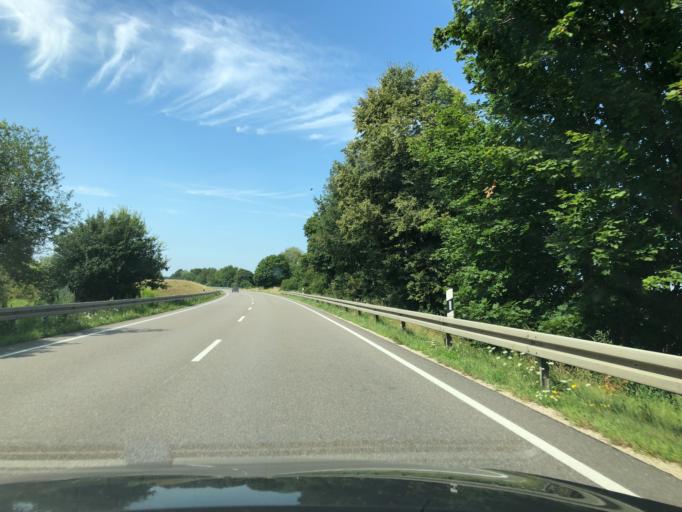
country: DE
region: Bavaria
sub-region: Upper Bavaria
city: Burgheim
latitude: 48.7154
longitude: 11.0496
